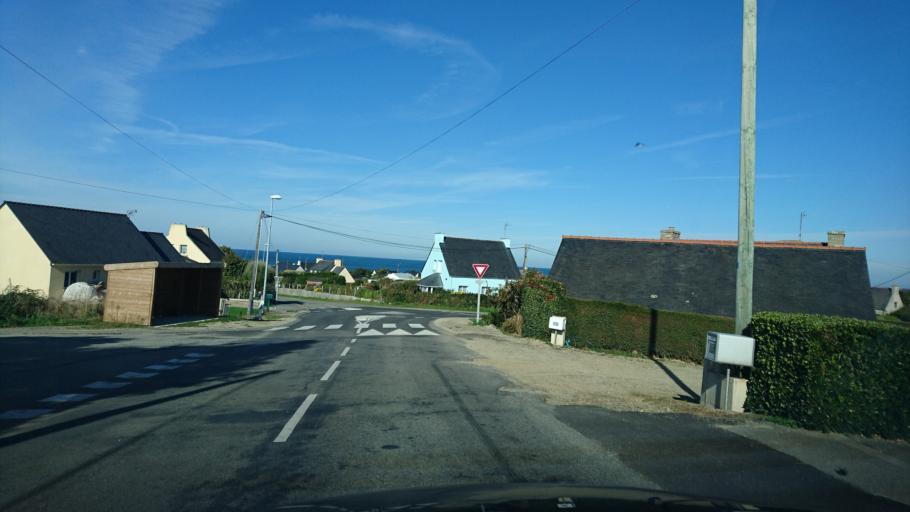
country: FR
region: Brittany
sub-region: Departement du Finistere
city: Lampaul-Plouarzel
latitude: 48.4358
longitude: -4.7742
